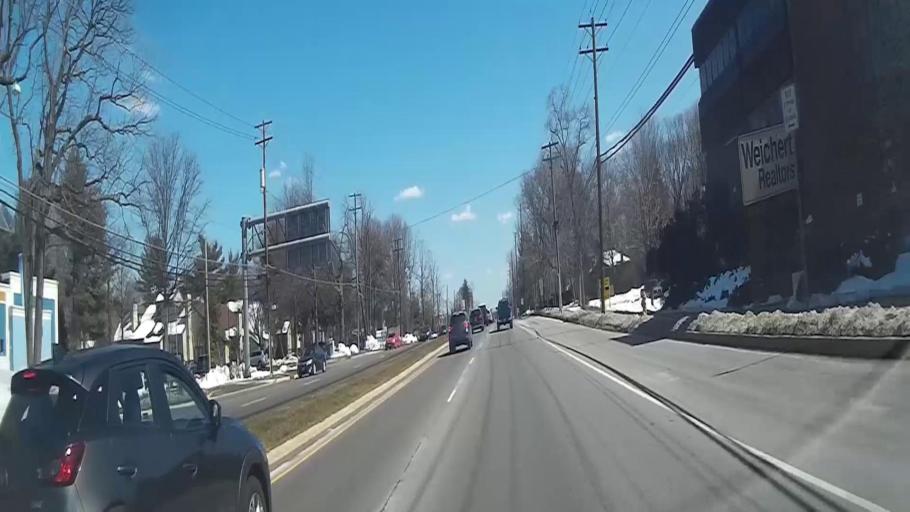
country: US
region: New Jersey
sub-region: Camden County
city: Springdale
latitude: 39.9021
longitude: -74.9649
